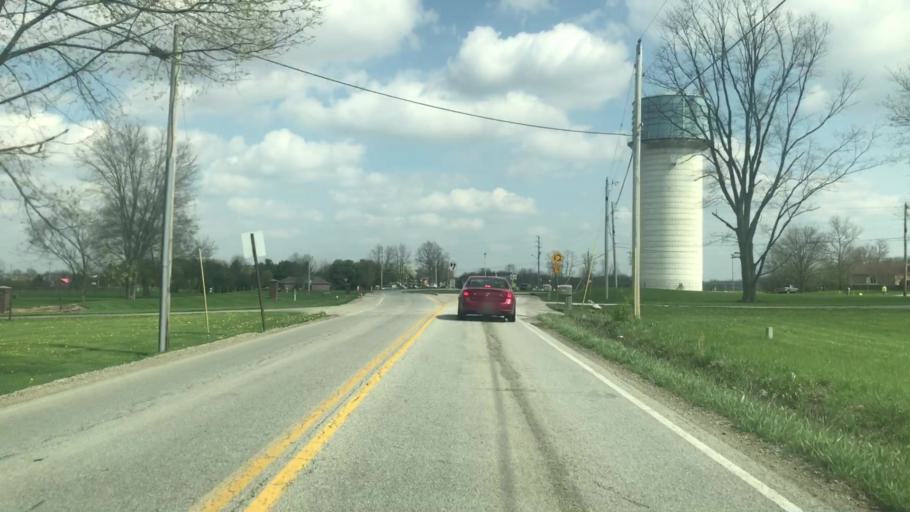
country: US
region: Indiana
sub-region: Johnson County
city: Waterloo
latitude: 39.5485
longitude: -86.2048
